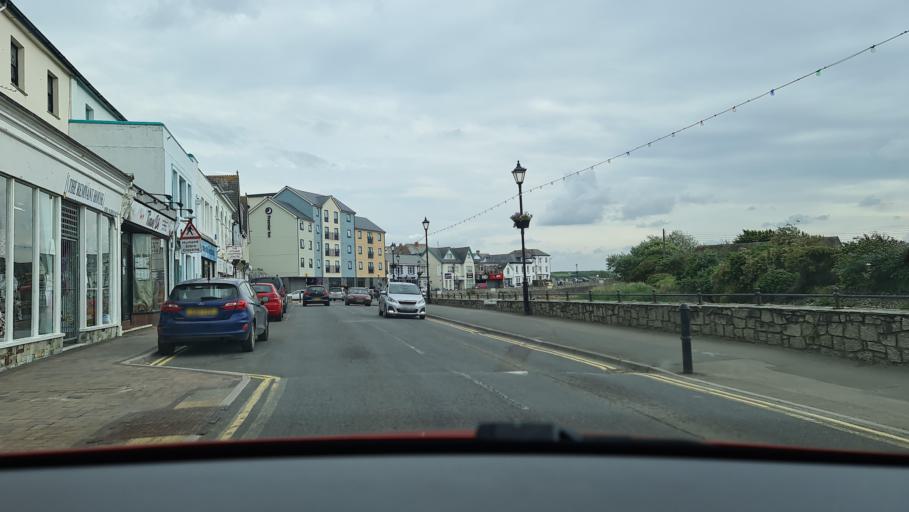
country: GB
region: England
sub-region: Cornwall
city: Bude
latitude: 50.8287
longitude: -4.5447
